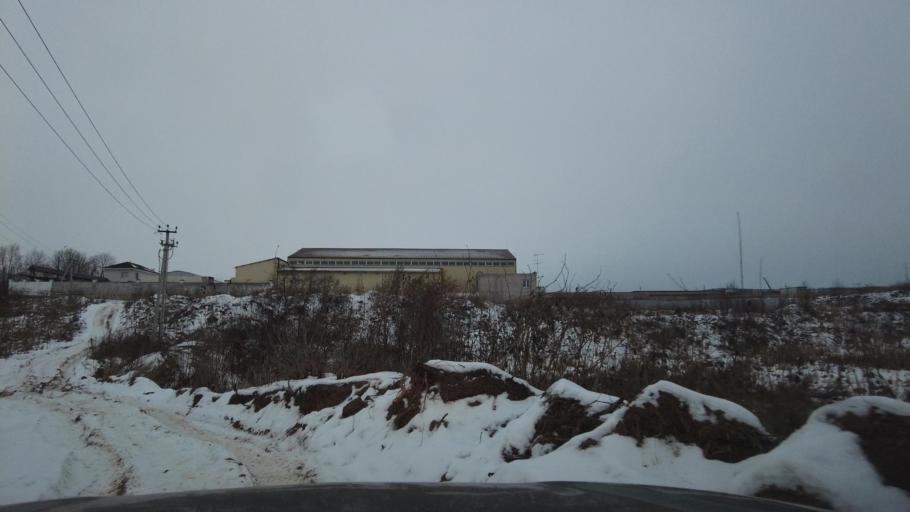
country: RU
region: Moskovskaya
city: Novopodrezkovo
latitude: 55.9899
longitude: 37.3935
